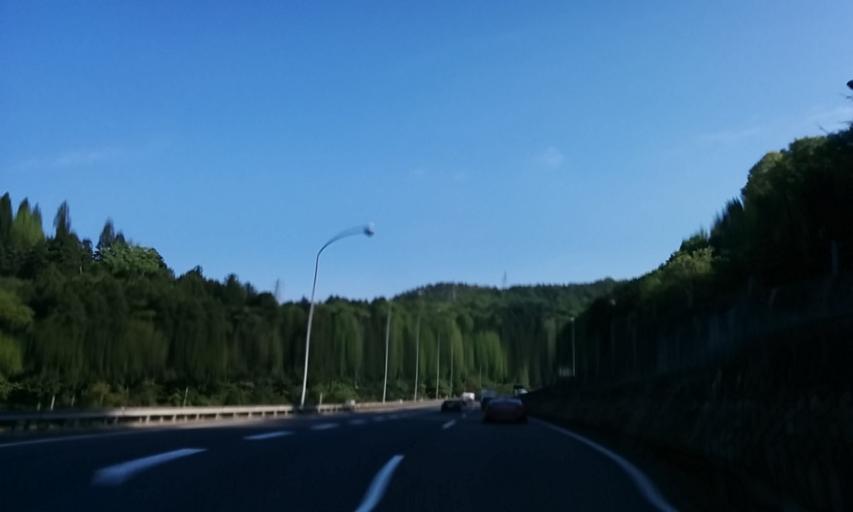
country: JP
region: Shiga Prefecture
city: Hikone
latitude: 35.2920
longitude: 136.2981
